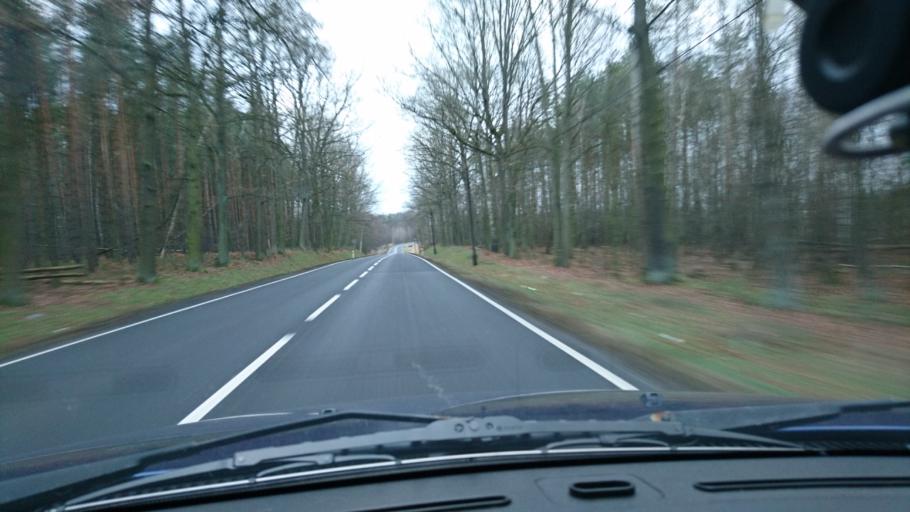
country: PL
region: Opole Voivodeship
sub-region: Powiat kluczborski
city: Kluczbork
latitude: 50.9510
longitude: 18.3121
